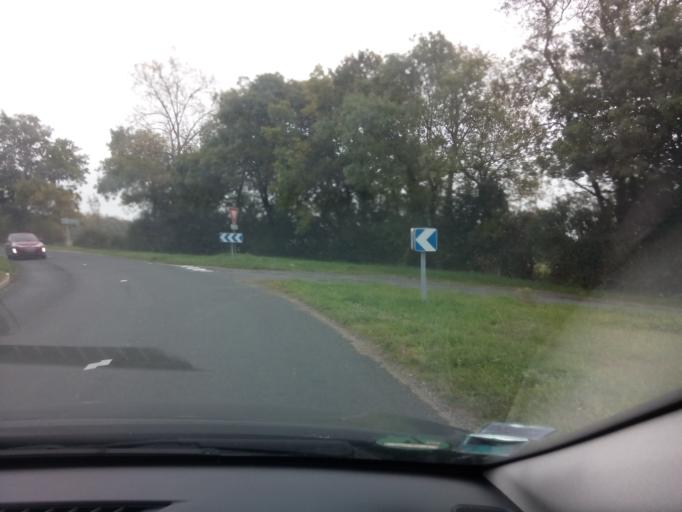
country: FR
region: Pays de la Loire
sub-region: Departement de Maine-et-Loire
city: Soulaire-et-Bourg
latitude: 47.6158
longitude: -0.5284
